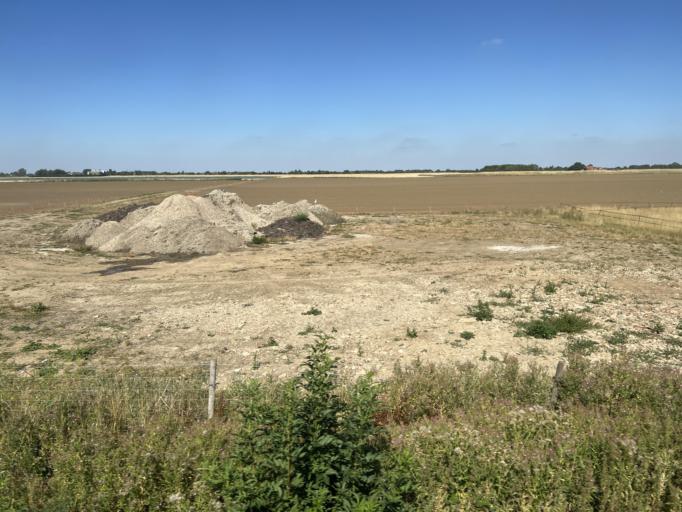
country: GB
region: England
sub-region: Lincolnshire
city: Boston
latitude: 53.0162
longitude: 0.0023
